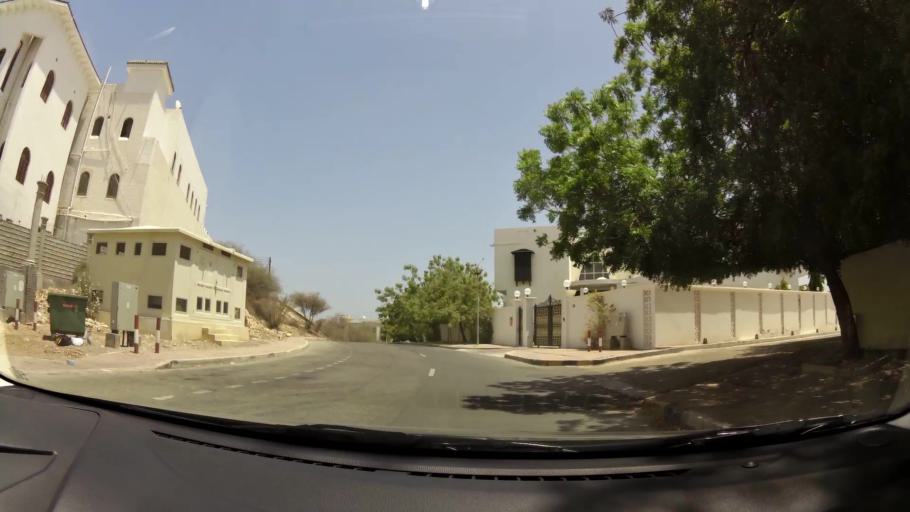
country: OM
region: Muhafazat Masqat
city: Bawshar
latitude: 23.6082
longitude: 58.4754
